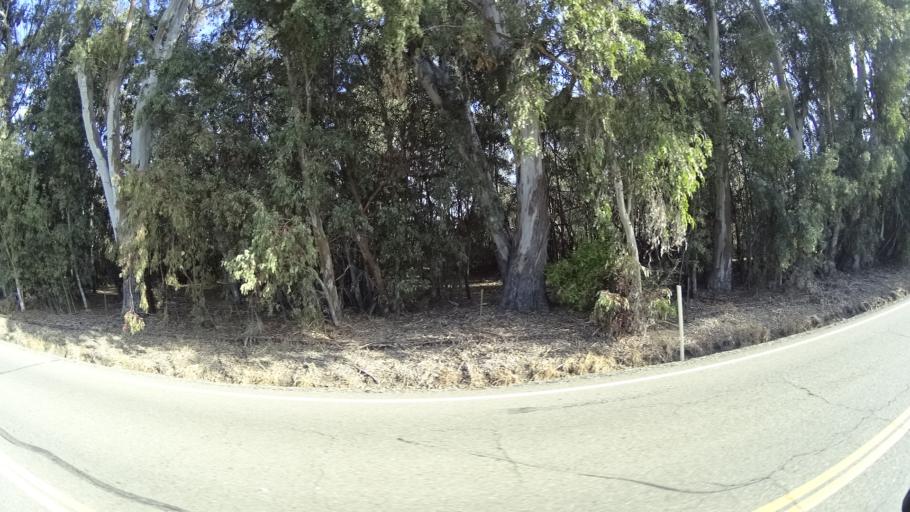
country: US
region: California
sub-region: Glenn County
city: Willows
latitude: 39.5823
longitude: -122.1991
